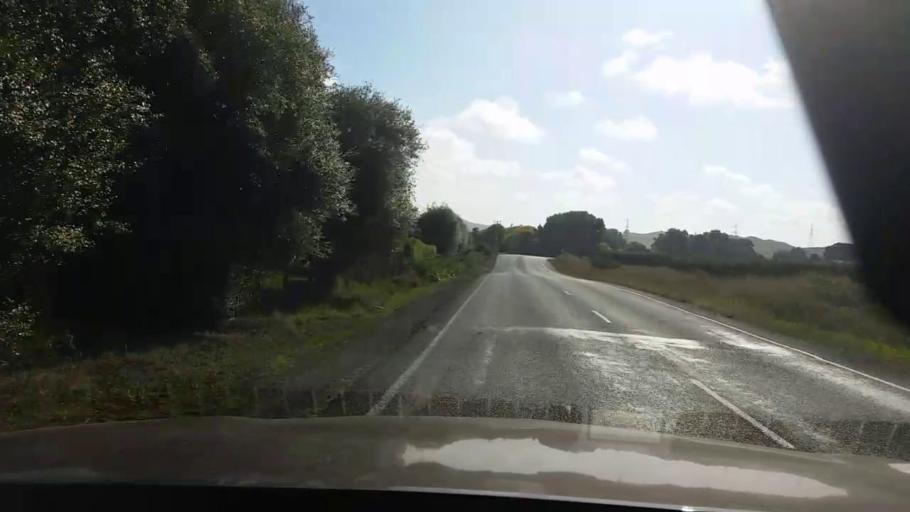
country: NZ
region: Waikato
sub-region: Hamilton City
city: Hamilton
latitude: -37.5894
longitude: 175.3887
